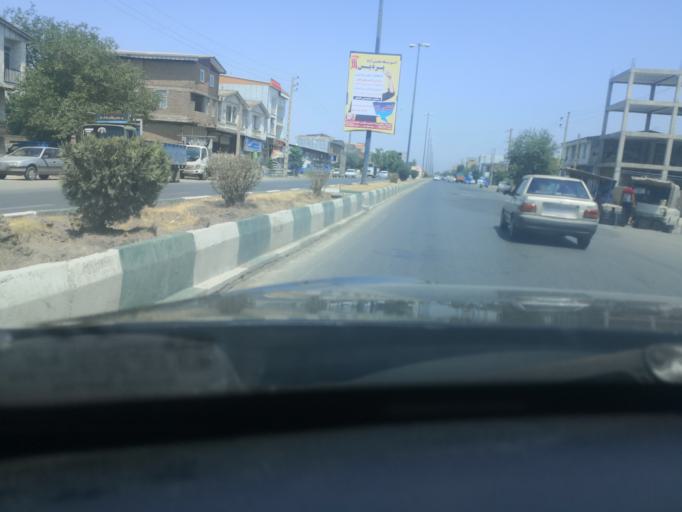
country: IR
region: Golestan
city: Aq Qala
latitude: 37.0092
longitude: 54.4637
